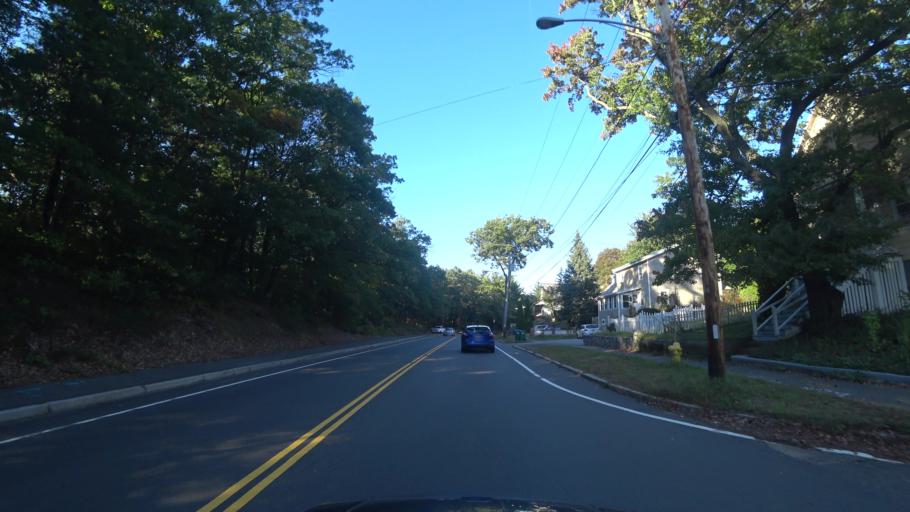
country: US
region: Massachusetts
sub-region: Middlesex County
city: Medford
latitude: 42.4398
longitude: -71.0971
